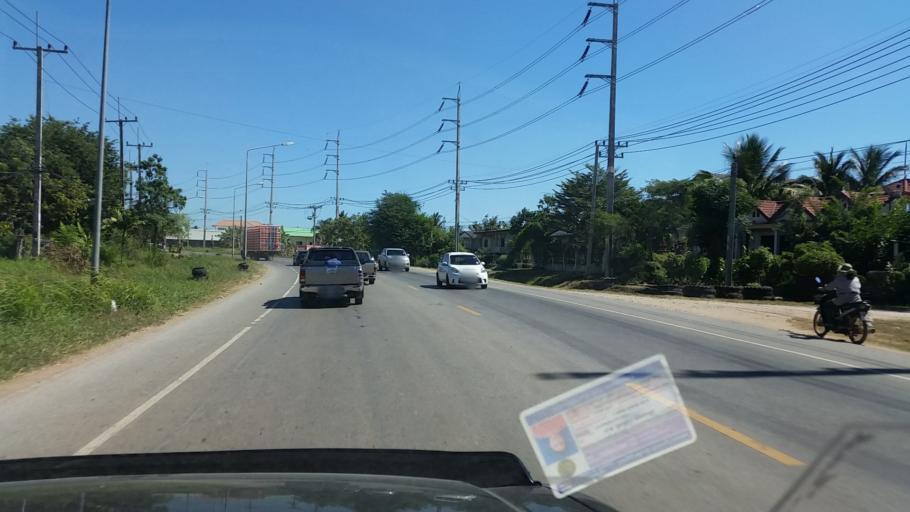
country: TH
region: Chaiyaphum
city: Ban Khwao
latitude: 15.7811
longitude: 101.8969
